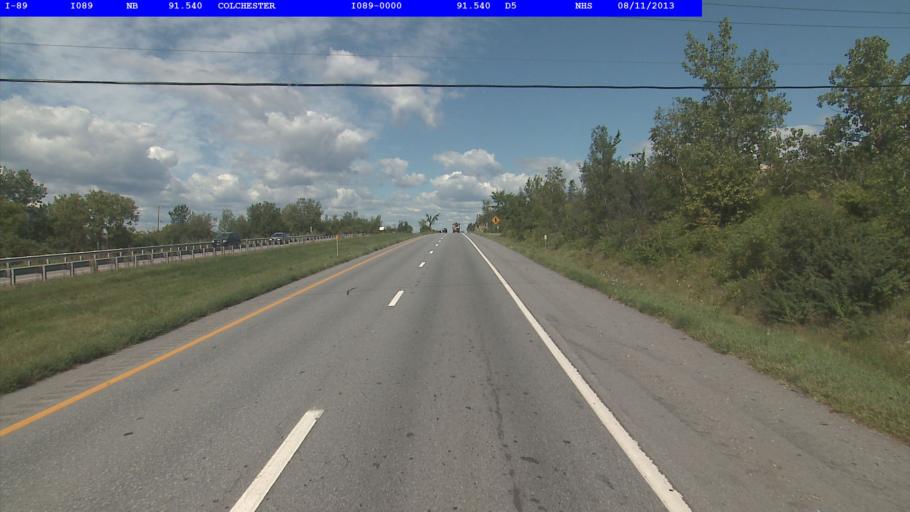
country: US
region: Vermont
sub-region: Chittenden County
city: Winooski
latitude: 44.5060
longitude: -73.1818
